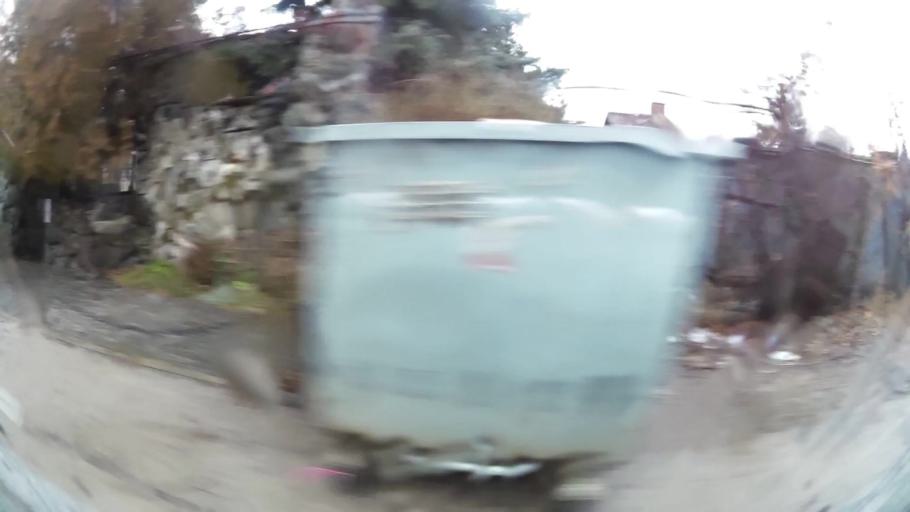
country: BG
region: Sofia-Capital
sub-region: Stolichna Obshtina
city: Sofia
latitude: 42.6464
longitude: 23.3321
